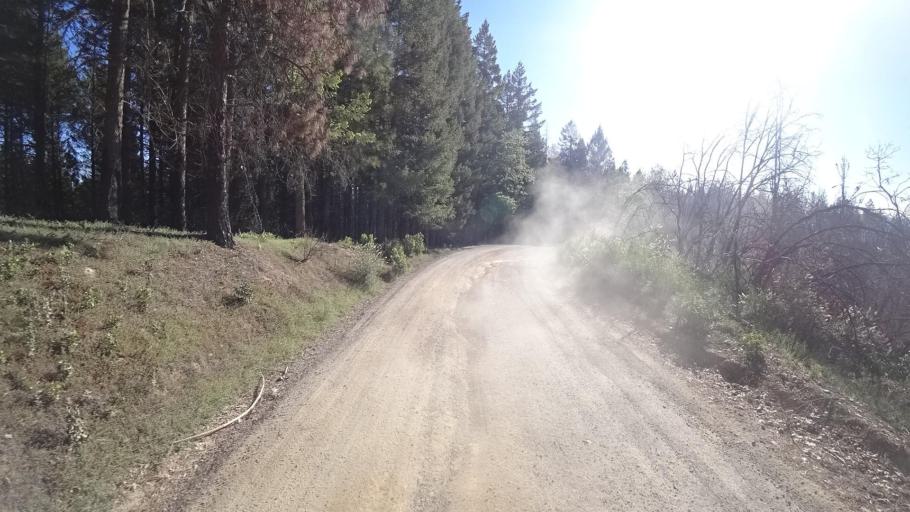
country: US
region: California
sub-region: Lake County
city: Upper Lake
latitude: 39.3459
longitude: -122.9678
